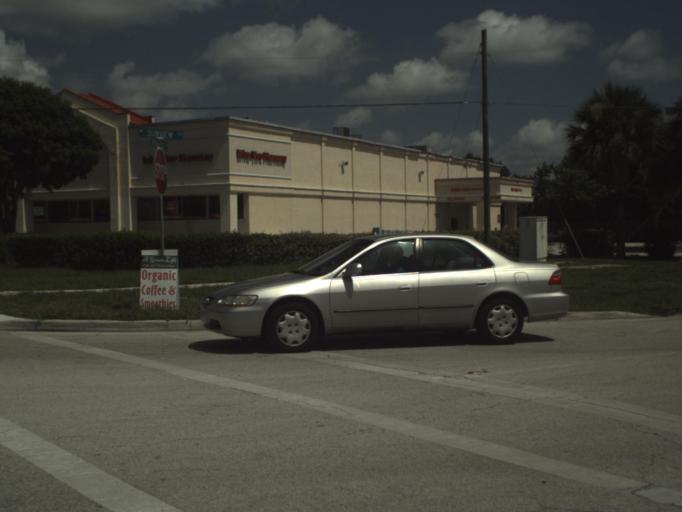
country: US
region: Florida
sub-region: Martin County
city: Jensen Beach
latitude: 27.2448
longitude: -80.2352
